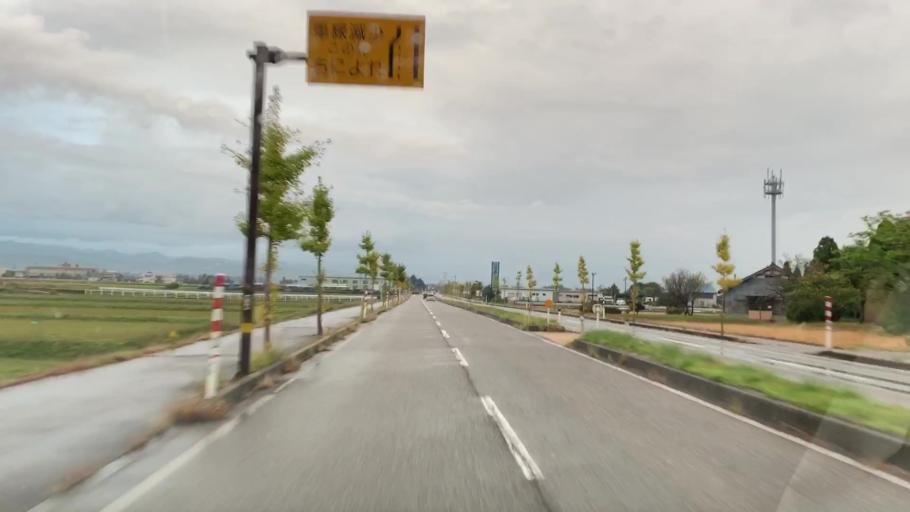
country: JP
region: Toyama
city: Kamiichi
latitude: 36.6750
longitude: 137.3274
